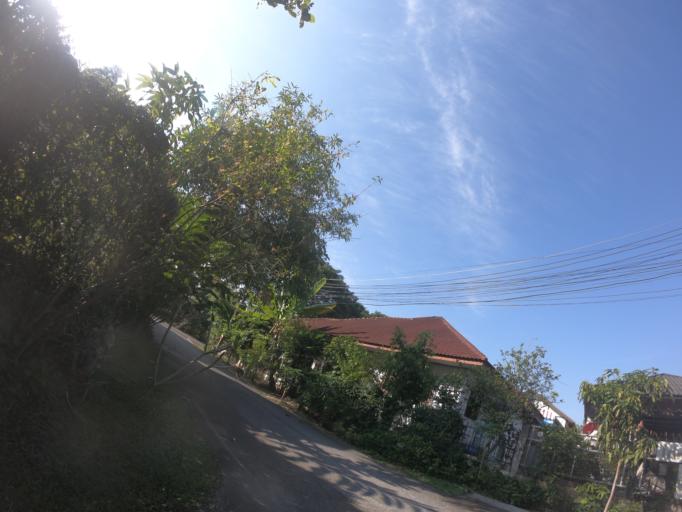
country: TH
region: Chiang Mai
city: Chiang Mai
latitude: 18.7791
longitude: 99.0335
